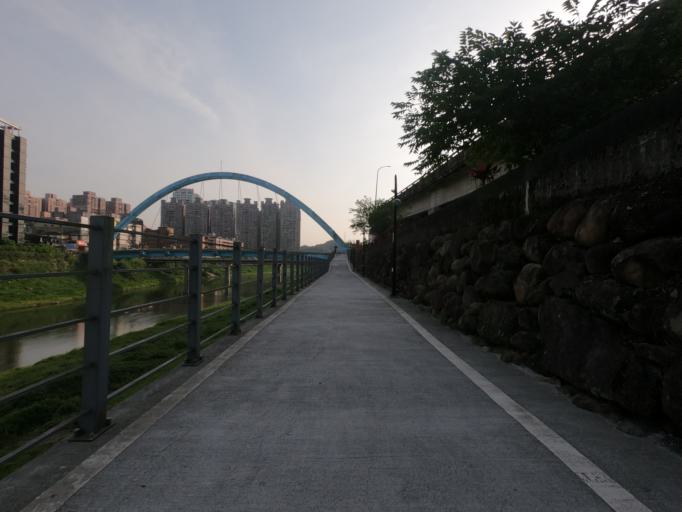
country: TW
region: Taiwan
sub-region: Keelung
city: Keelung
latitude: 25.0699
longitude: 121.6569
